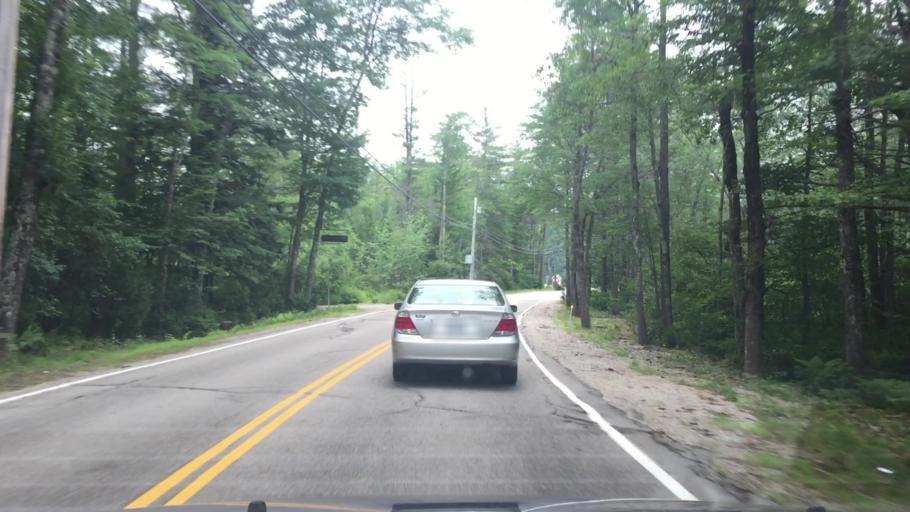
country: US
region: New Hampshire
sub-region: Carroll County
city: Madison
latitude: 43.9162
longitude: -71.0732
